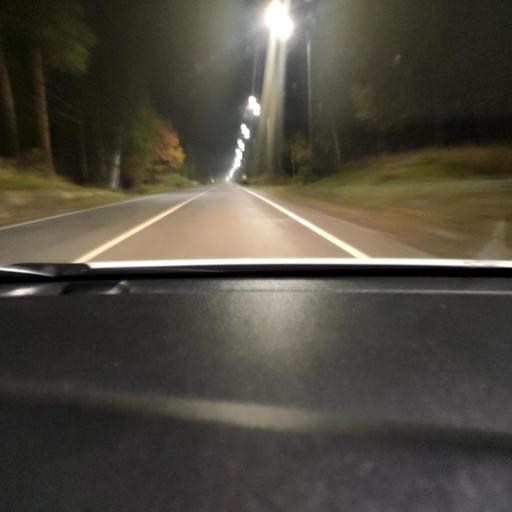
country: RU
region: Tatarstan
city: Verkhniy Uslon
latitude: 55.6368
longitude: 49.0591
